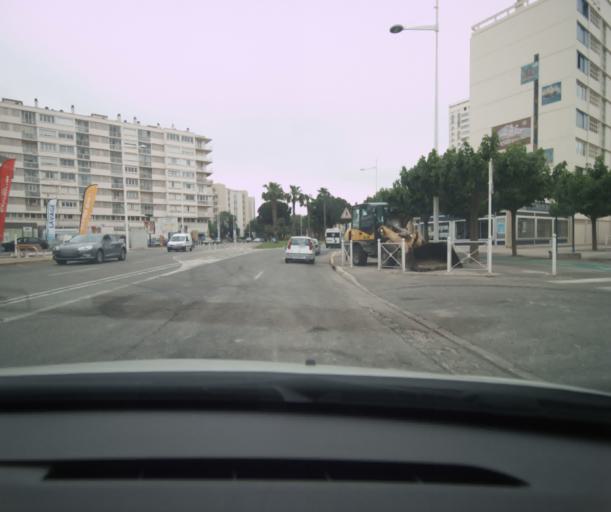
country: FR
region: Provence-Alpes-Cote d'Azur
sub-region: Departement du Var
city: Toulon
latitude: 43.1133
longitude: 5.9346
